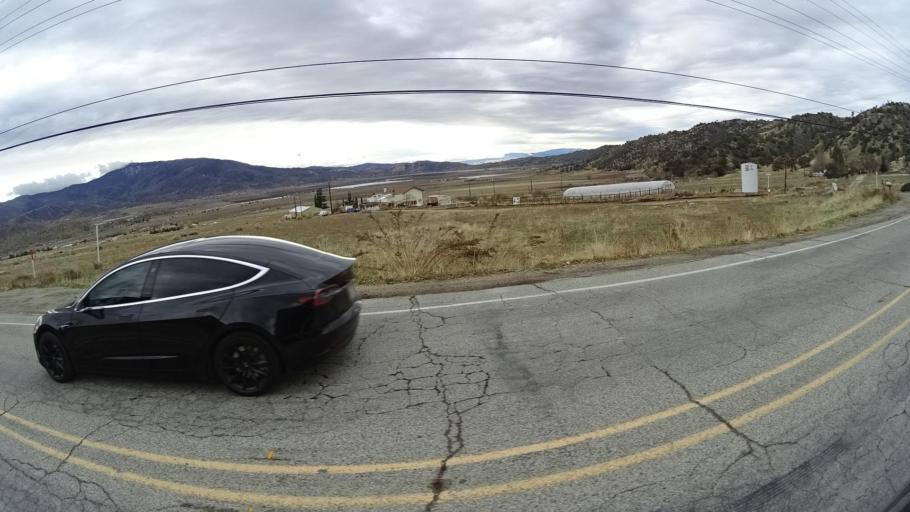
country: US
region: California
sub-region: Kern County
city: Bear Valley Springs
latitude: 35.1467
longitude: -118.5756
